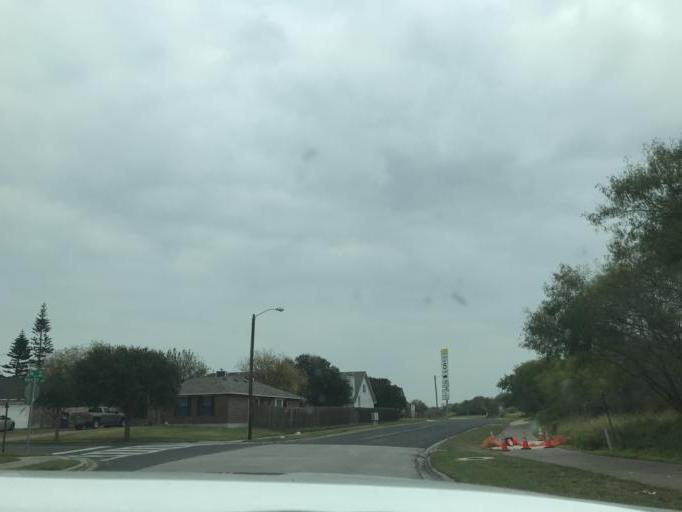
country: US
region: Texas
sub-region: Nueces County
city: Corpus Christi
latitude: 27.6677
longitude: -97.3463
